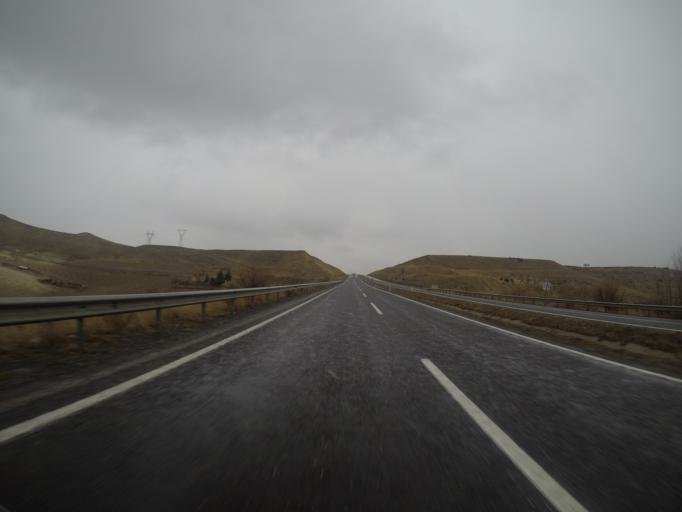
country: TR
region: Nevsehir
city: Urgub
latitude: 38.7420
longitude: 35.0100
